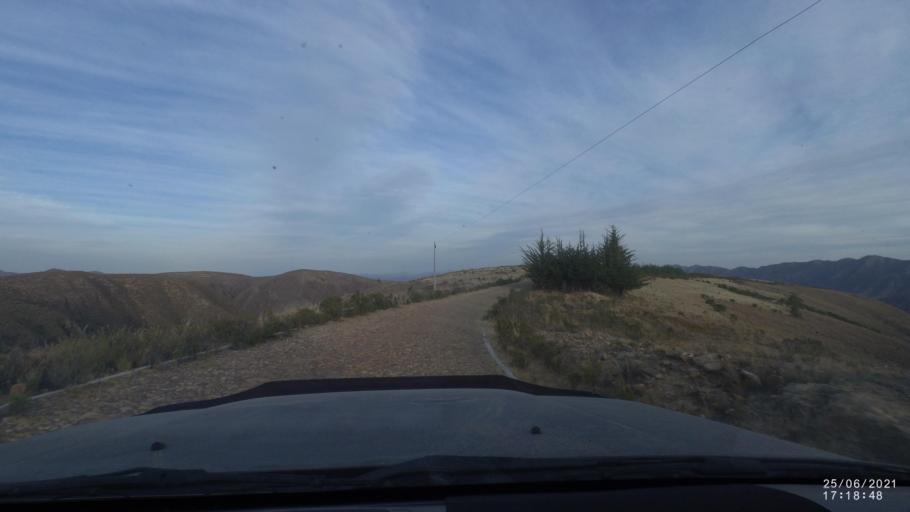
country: BO
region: Cochabamba
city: Arani
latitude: -17.8963
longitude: -65.6932
